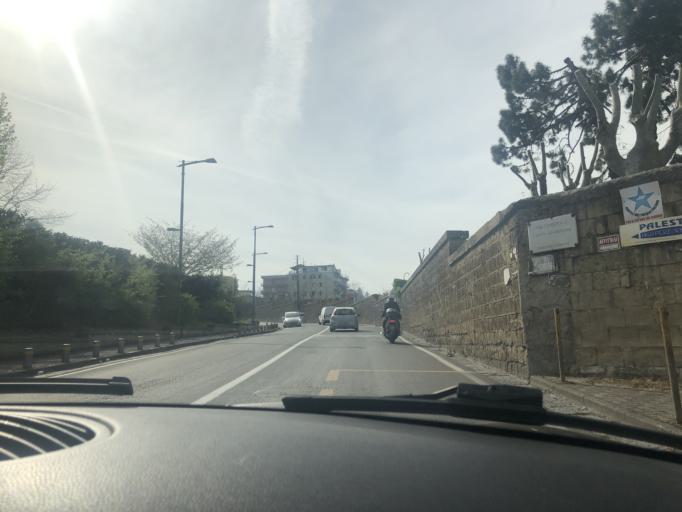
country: IT
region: Campania
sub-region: Provincia di Napoli
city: Torre Caracciolo
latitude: 40.8681
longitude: 14.2062
